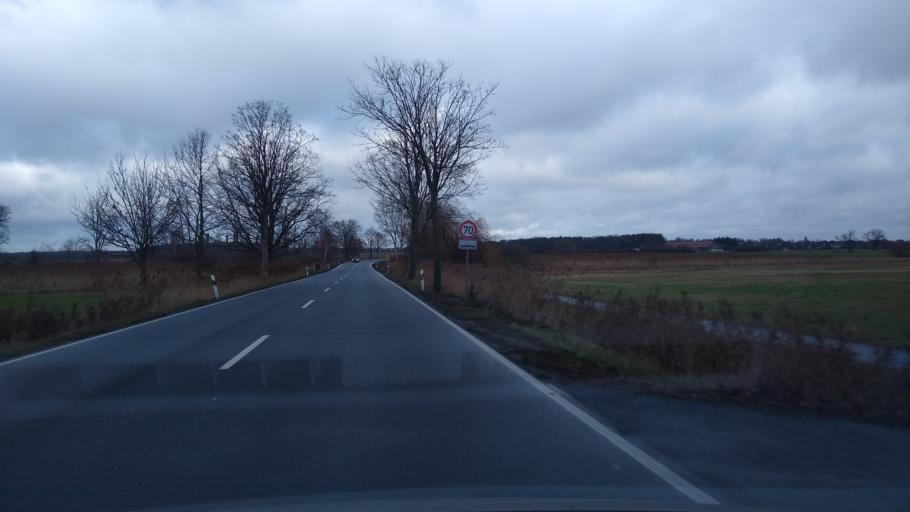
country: DE
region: Lower Saxony
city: Edemissen
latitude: 52.3705
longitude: 10.2493
